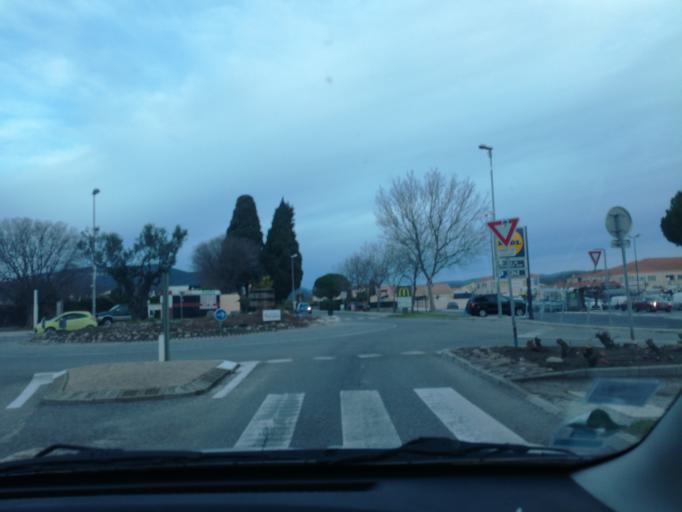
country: FR
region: Provence-Alpes-Cote d'Azur
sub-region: Departement du Var
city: La Crau
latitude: 43.1522
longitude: 6.0726
